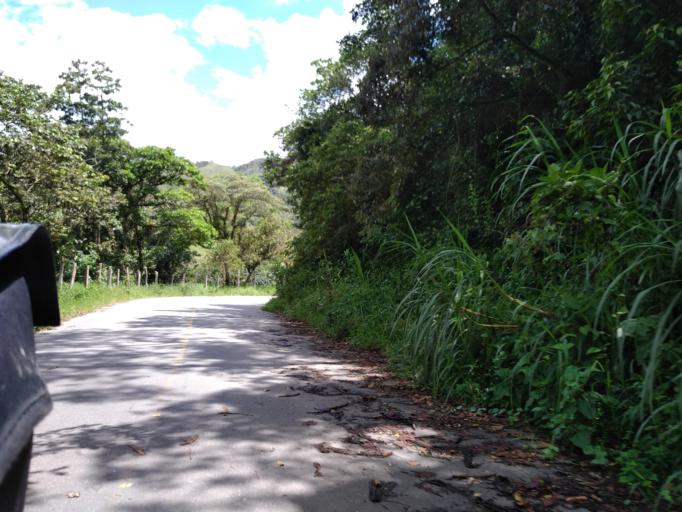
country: CO
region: Santander
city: Oiba
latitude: 6.1886
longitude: -73.1822
